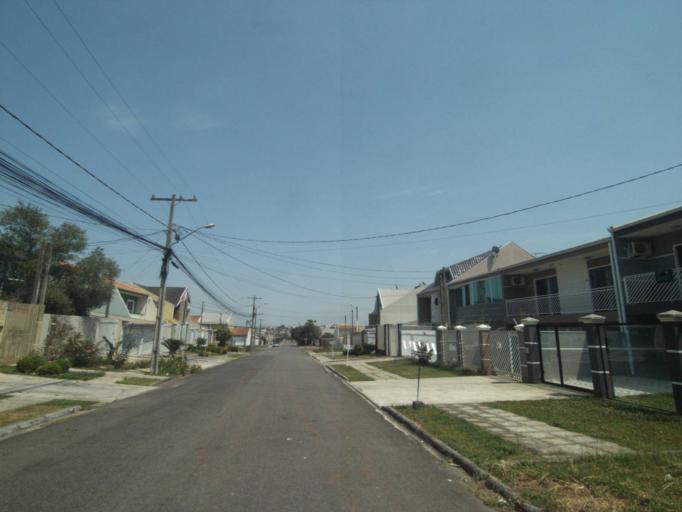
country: BR
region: Parana
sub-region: Sao Jose Dos Pinhais
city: Sao Jose dos Pinhais
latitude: -25.5154
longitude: -49.2635
